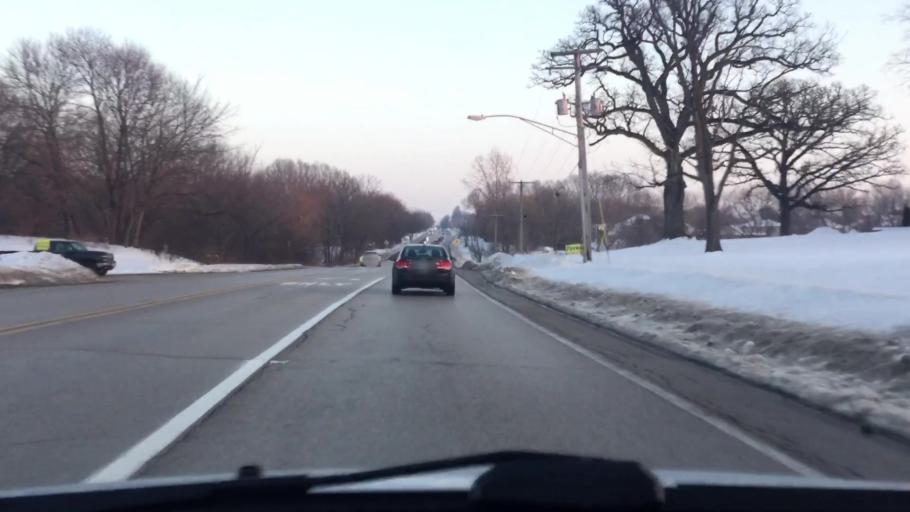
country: US
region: Illinois
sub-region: Kane County
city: Village of Campton Hills
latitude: 41.9327
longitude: -88.3823
